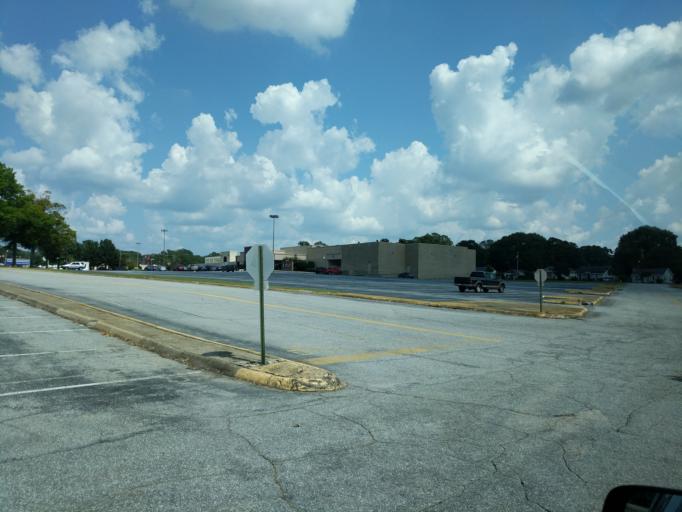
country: US
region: South Carolina
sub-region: Greenville County
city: Greenville
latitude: 34.8395
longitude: -82.3623
